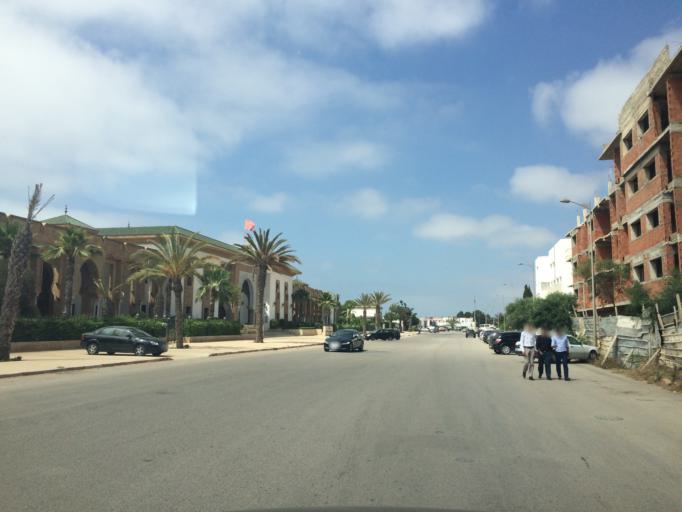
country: MA
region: Rabat-Sale-Zemmour-Zaer
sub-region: Skhirate-Temara
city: Temara
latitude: 33.9642
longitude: -6.8816
